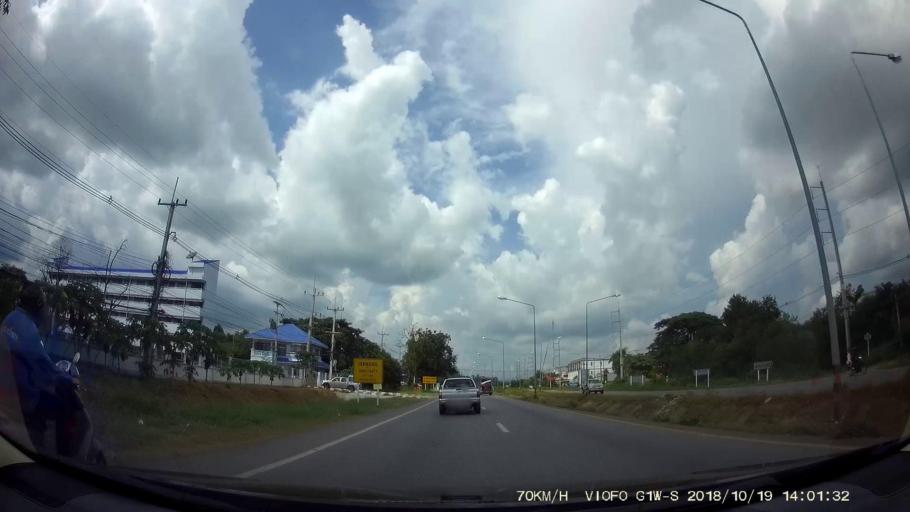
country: TH
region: Chaiyaphum
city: Chaiyaphum
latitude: 15.8304
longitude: 102.0586
